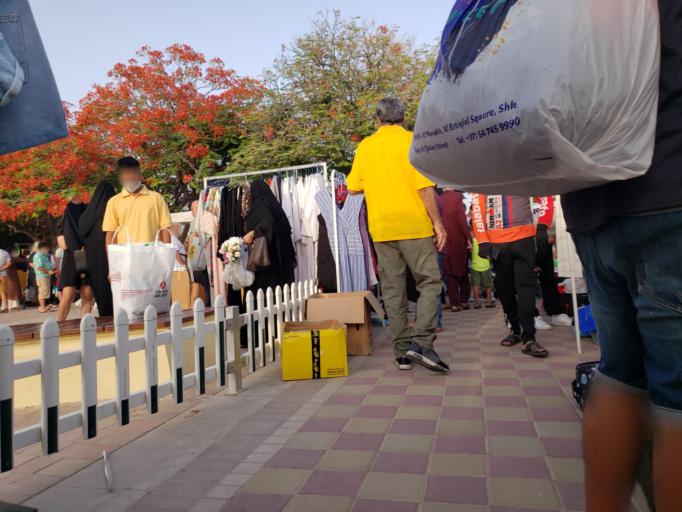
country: AE
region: Dubai
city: Dubai
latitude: 25.1028
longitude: 55.2021
